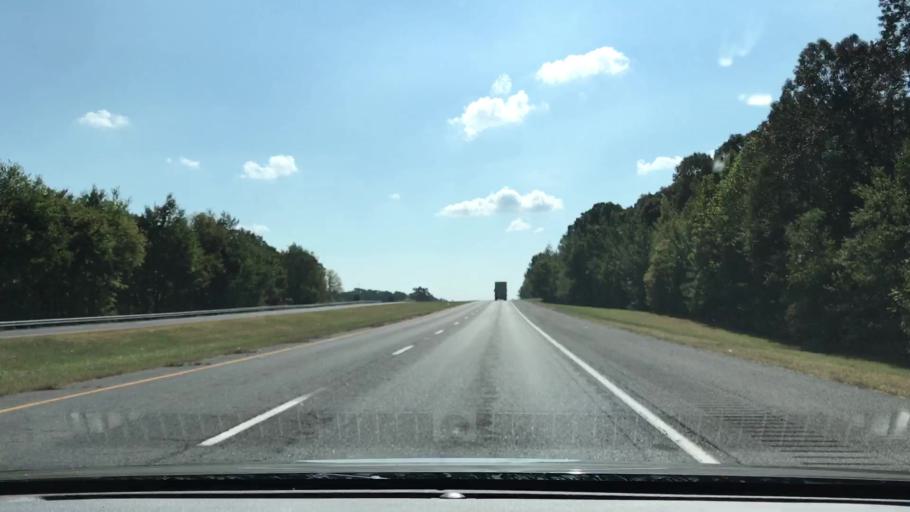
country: US
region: Kentucky
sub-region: Marshall County
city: Benton
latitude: 36.7733
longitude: -88.3177
